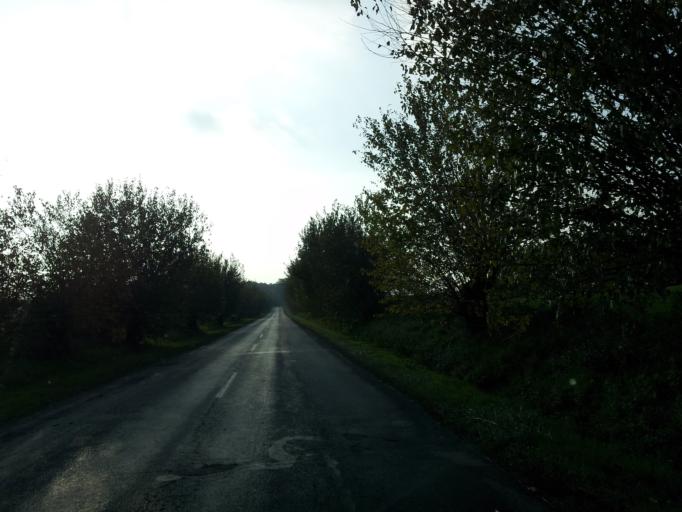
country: HU
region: Komarom-Esztergom
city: Csaszar
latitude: 47.4926
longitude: 18.1274
